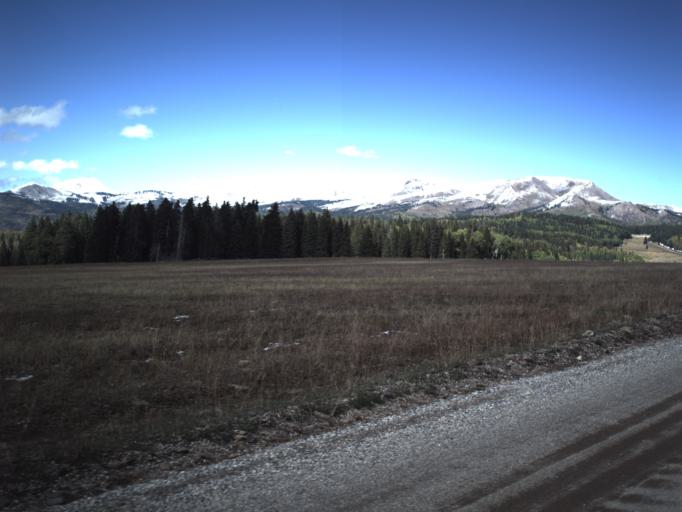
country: US
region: Utah
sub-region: Piute County
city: Junction
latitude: 38.2736
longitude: -112.3658
